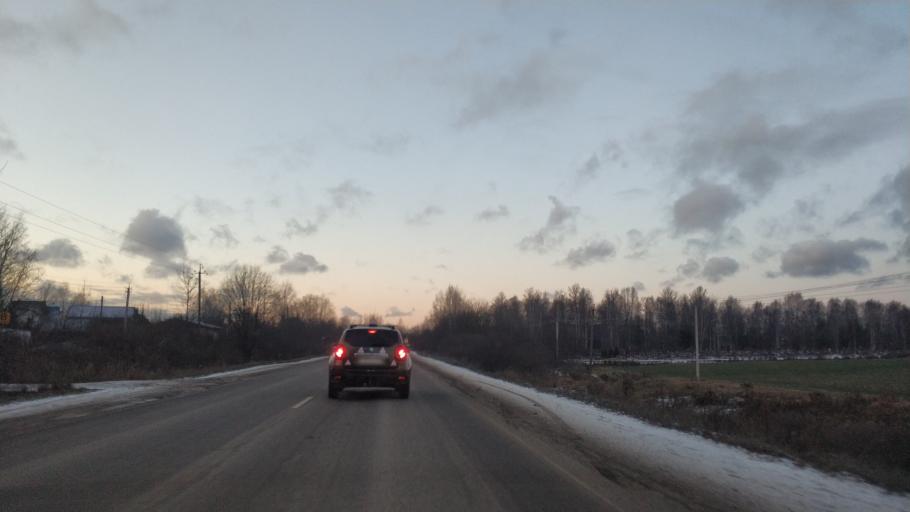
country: RU
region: St.-Petersburg
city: Pontonnyy
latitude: 59.8050
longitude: 30.6254
